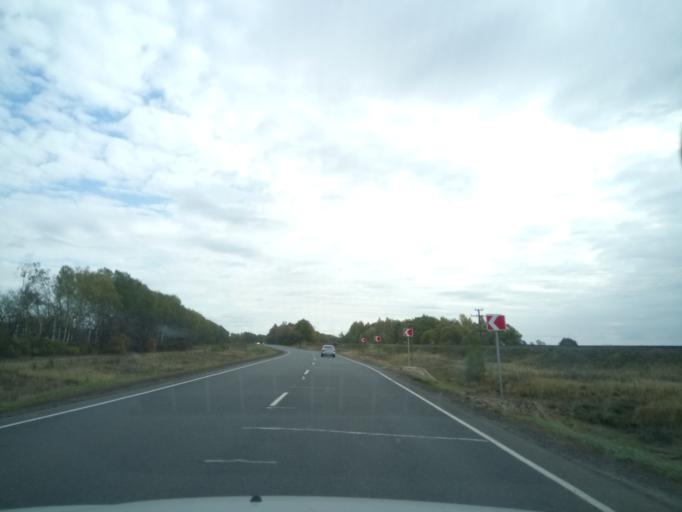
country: RU
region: Nizjnij Novgorod
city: Lukoyanov
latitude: 55.0654
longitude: 44.3496
